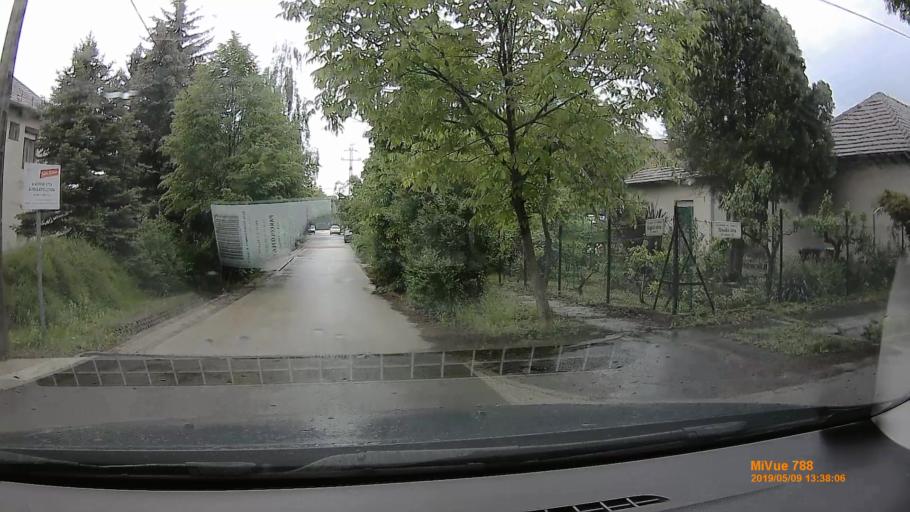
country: HU
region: Budapest
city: Budapest XVI. keruelet
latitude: 47.5298
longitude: 19.1983
